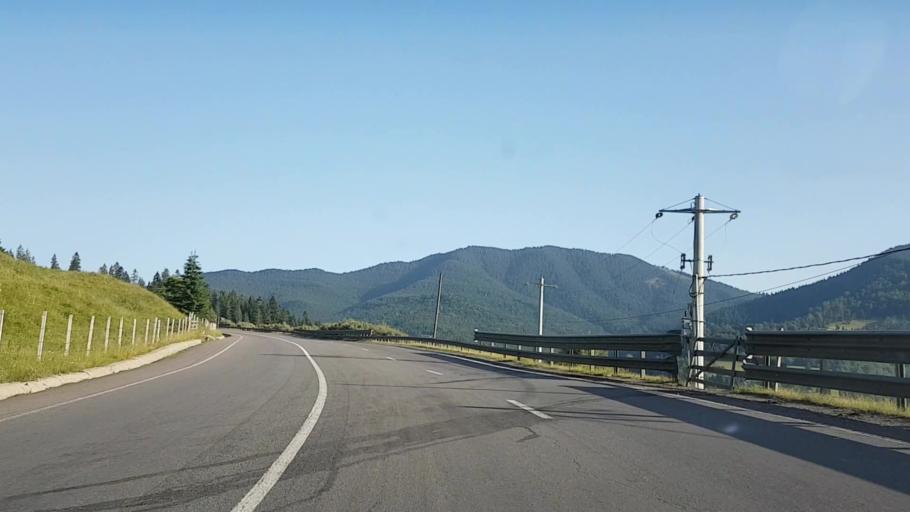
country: RO
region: Bistrita-Nasaud
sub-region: Comuna Lunca Ilvei
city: Lunca Ilvei
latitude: 47.2302
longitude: 24.9666
